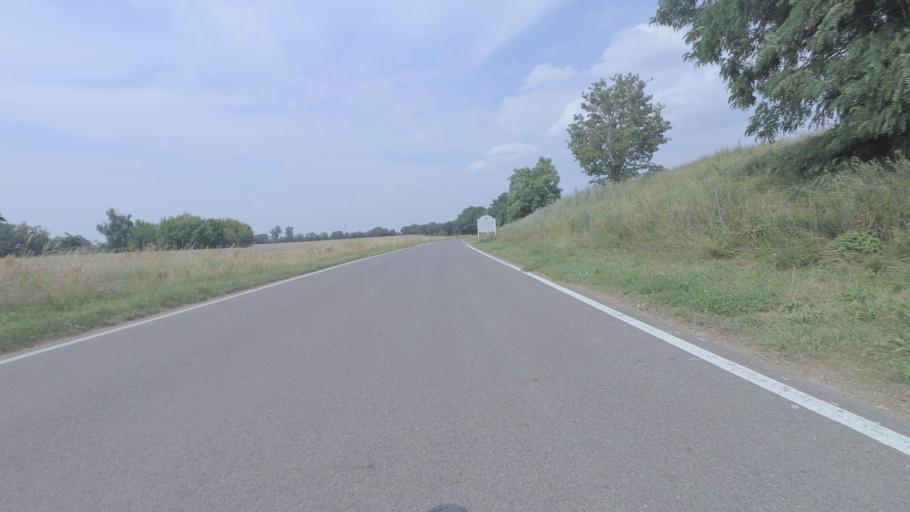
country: DE
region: Brandenburg
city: Rangsdorf
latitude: 52.3318
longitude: 13.4614
